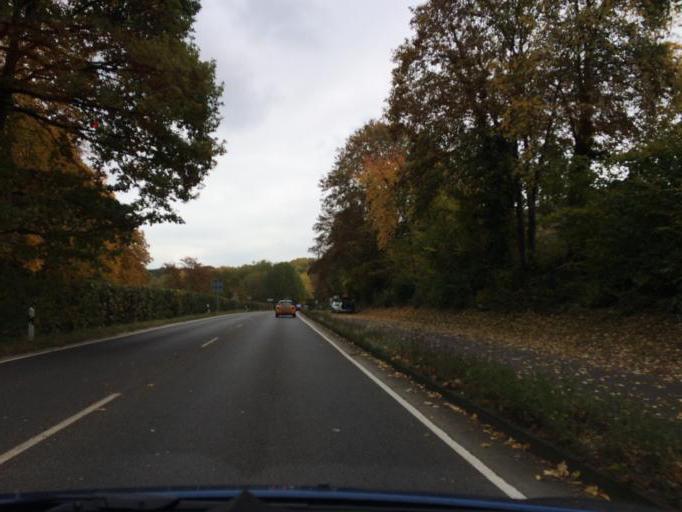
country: DE
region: North Rhine-Westphalia
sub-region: Regierungsbezirk Koln
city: Konigswinter
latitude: 50.6792
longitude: 7.2025
